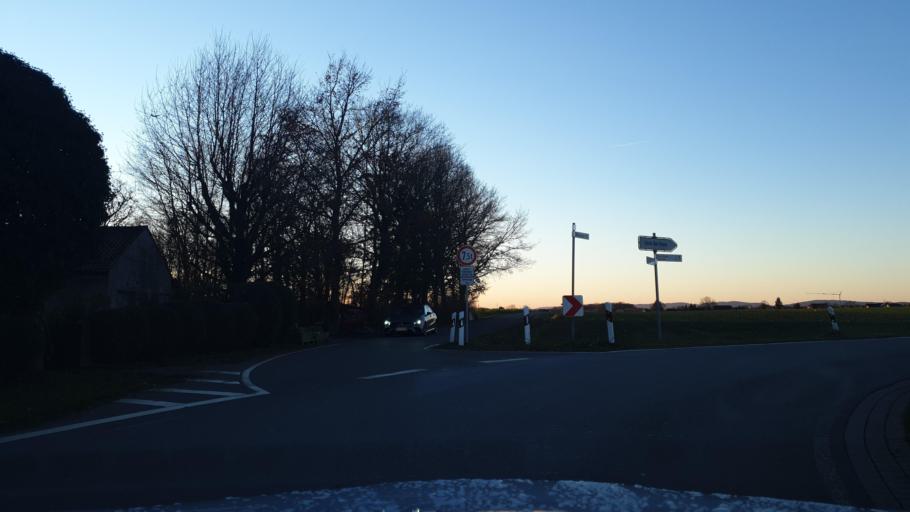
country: DE
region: North Rhine-Westphalia
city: Bad Oeynhausen
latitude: 52.2359
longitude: 8.8210
